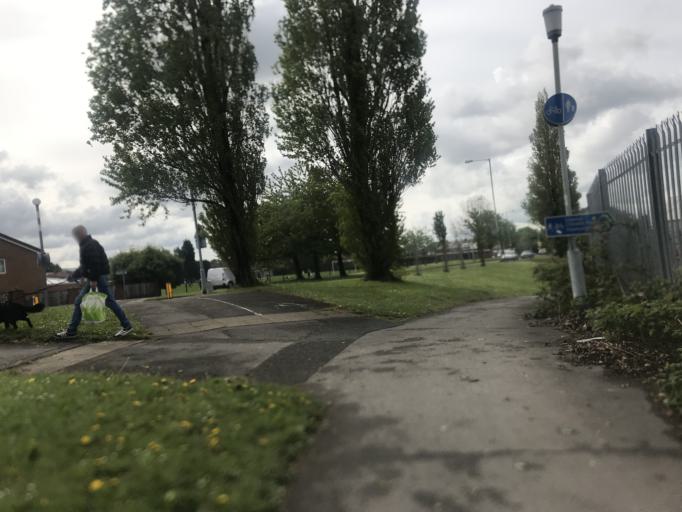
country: GB
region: England
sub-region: Borough of Stockport
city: Stockport
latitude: 53.3946
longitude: -2.1659
